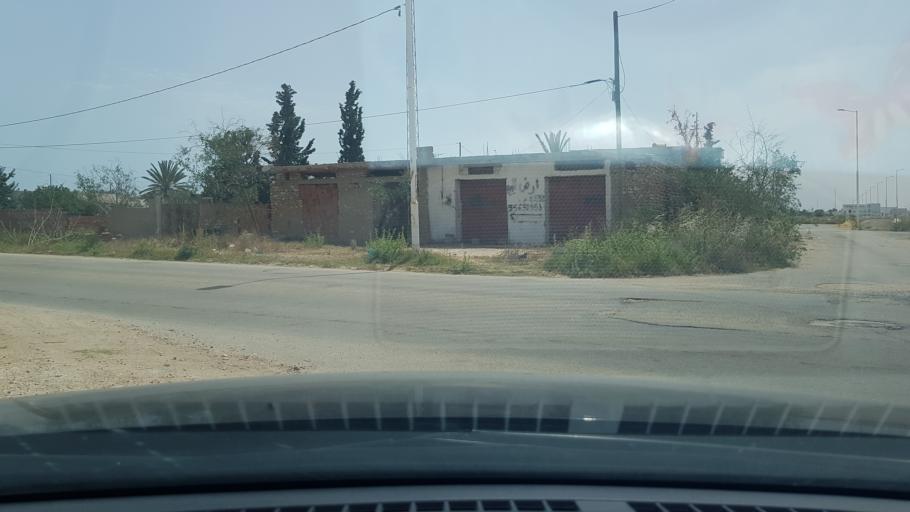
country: TN
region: Safaqis
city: Al Qarmadah
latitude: 34.8298
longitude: 10.7498
